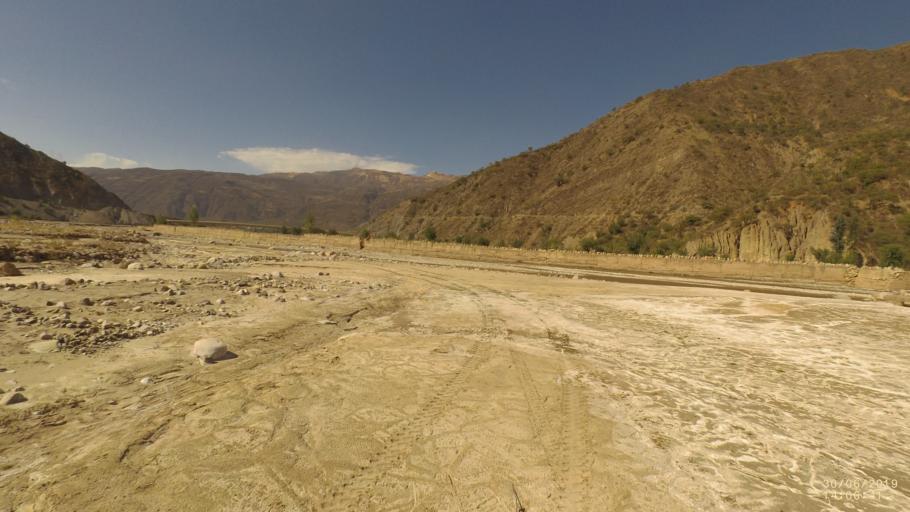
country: BO
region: Cochabamba
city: Irpa Irpa
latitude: -17.8031
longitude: -66.3551
